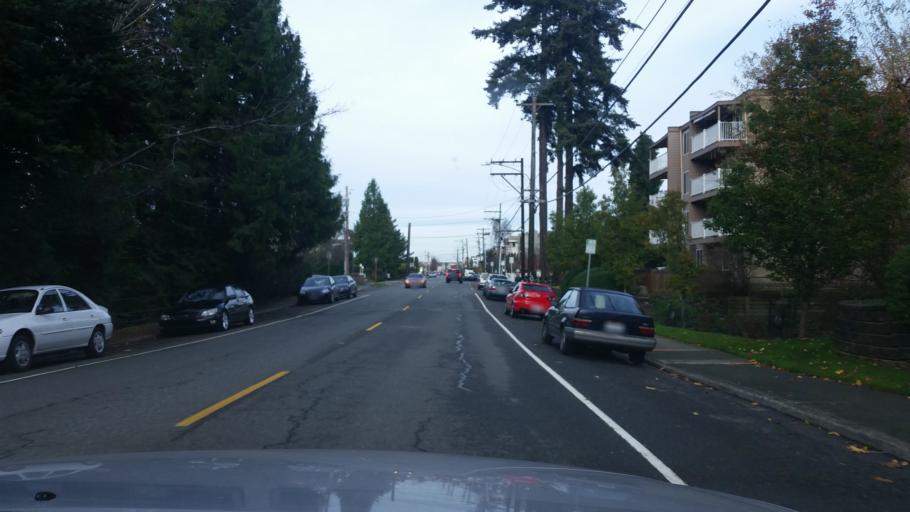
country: US
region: Washington
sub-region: Snohomish County
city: Edmonds
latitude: 47.8062
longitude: -122.3802
